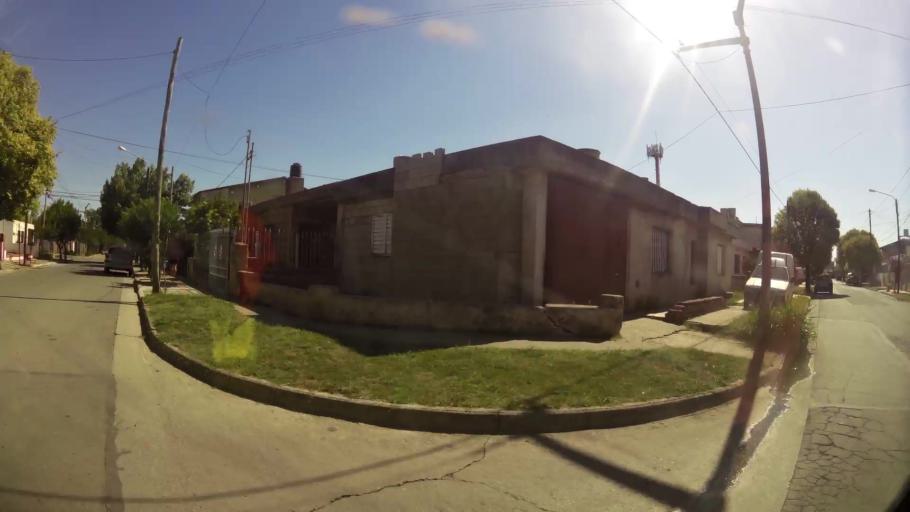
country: AR
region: Cordoba
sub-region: Departamento de Capital
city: Cordoba
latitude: -31.3610
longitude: -64.1669
